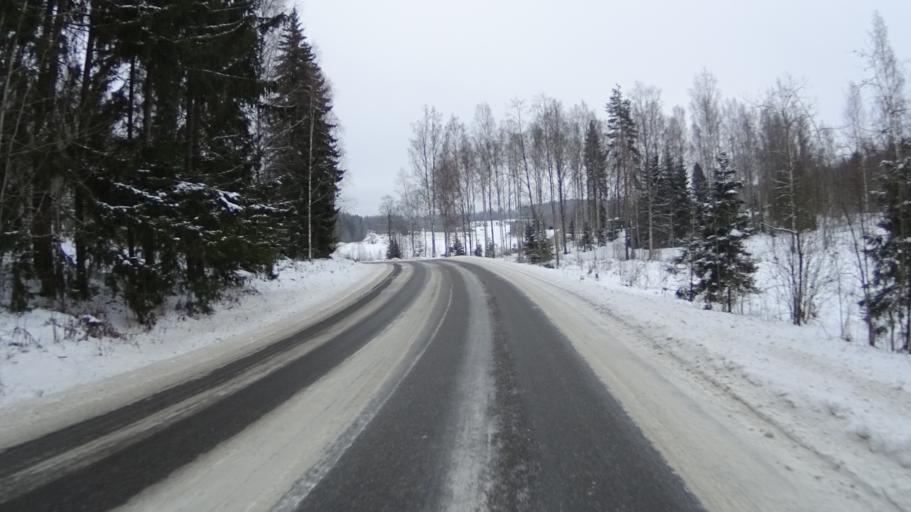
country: FI
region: Uusimaa
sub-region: Helsinki
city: Karkkila
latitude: 60.5120
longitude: 24.1596
